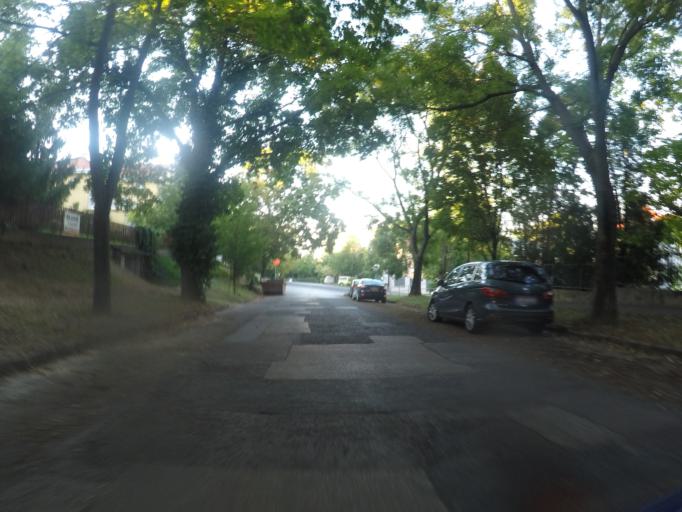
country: HU
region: Budapest
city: Budapest XII. keruelet
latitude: 47.5010
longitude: 19.0153
